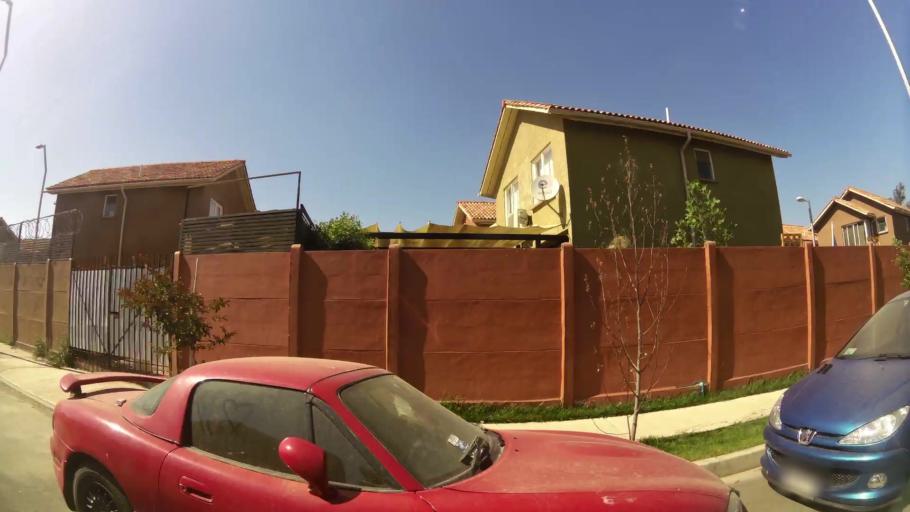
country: CL
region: Santiago Metropolitan
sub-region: Provincia de Maipo
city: San Bernardo
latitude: -33.6128
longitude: -70.6819
